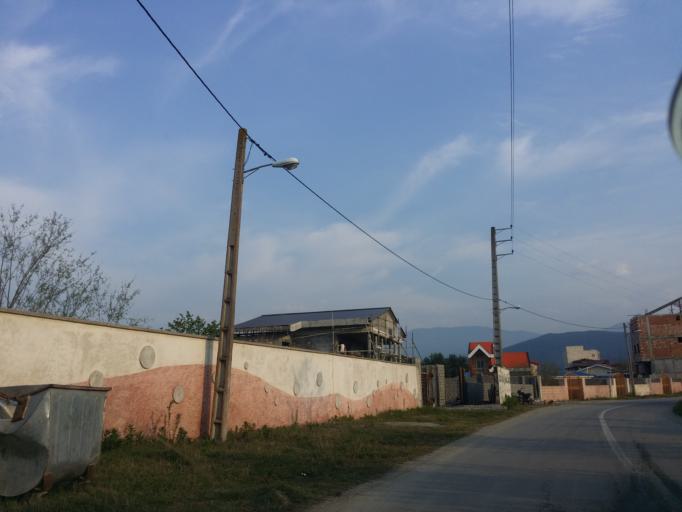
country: IR
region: Mazandaran
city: Chalus
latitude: 36.6818
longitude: 51.3720
